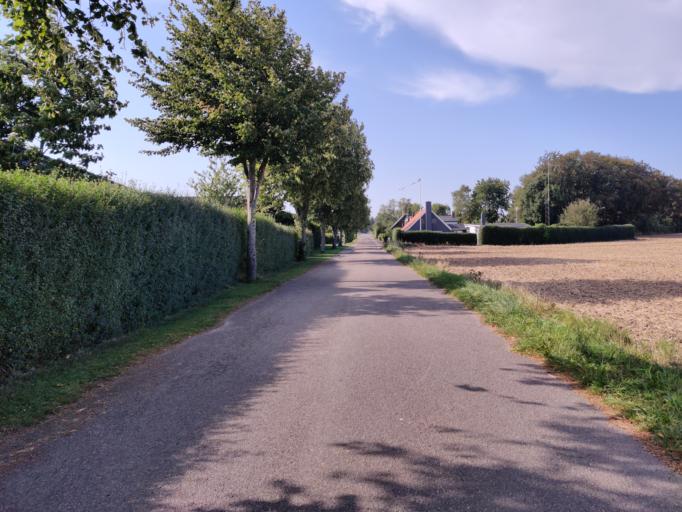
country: DK
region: Zealand
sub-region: Guldborgsund Kommune
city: Nykobing Falster
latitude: 54.7055
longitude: 11.9315
